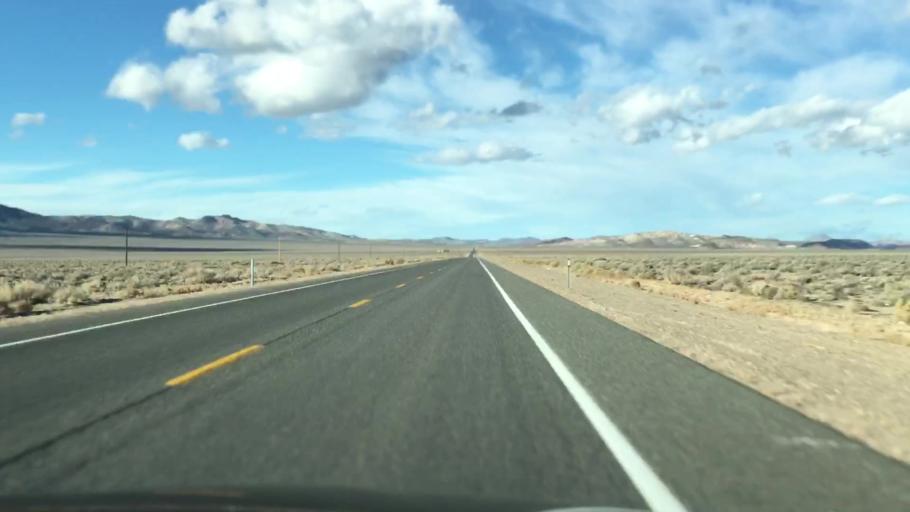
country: US
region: Nevada
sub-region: Esmeralda County
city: Goldfield
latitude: 37.4770
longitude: -117.1779
